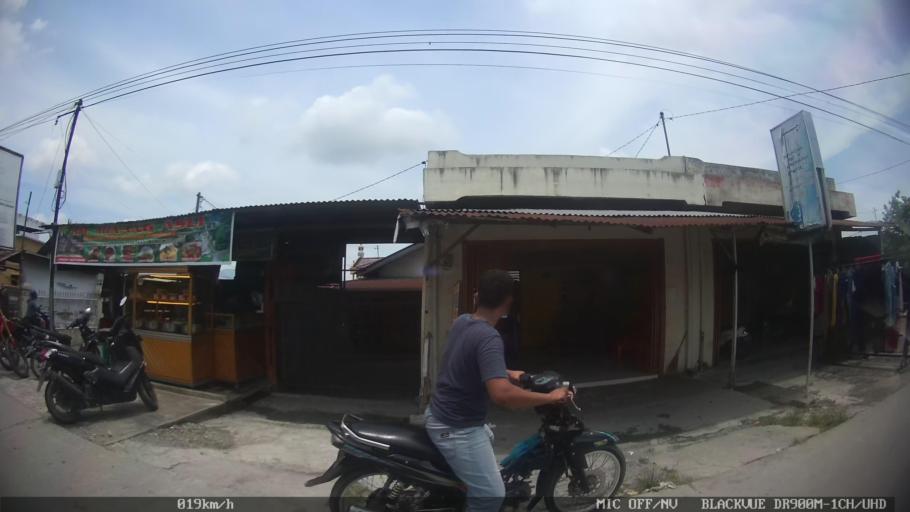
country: ID
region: North Sumatra
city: Labuhan Deli
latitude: 3.6910
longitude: 98.6826
